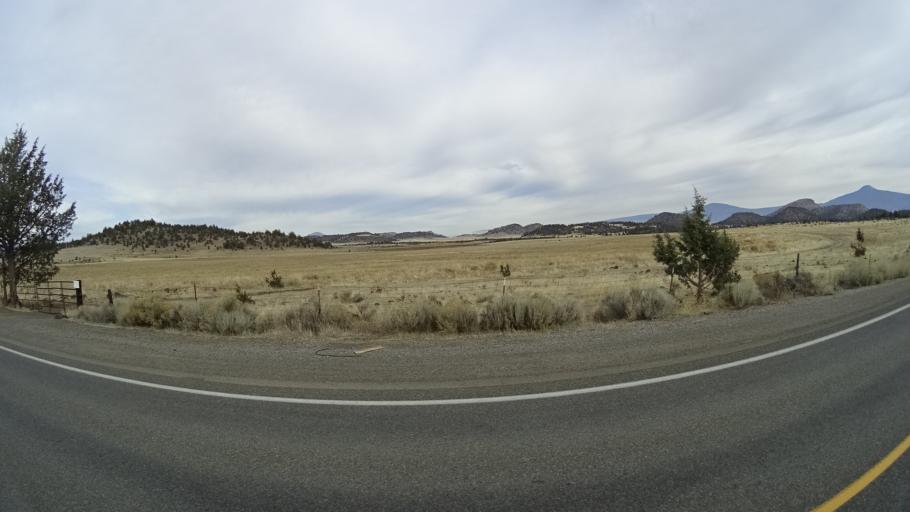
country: US
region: California
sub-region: Siskiyou County
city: Montague
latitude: 41.6404
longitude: -122.4732
